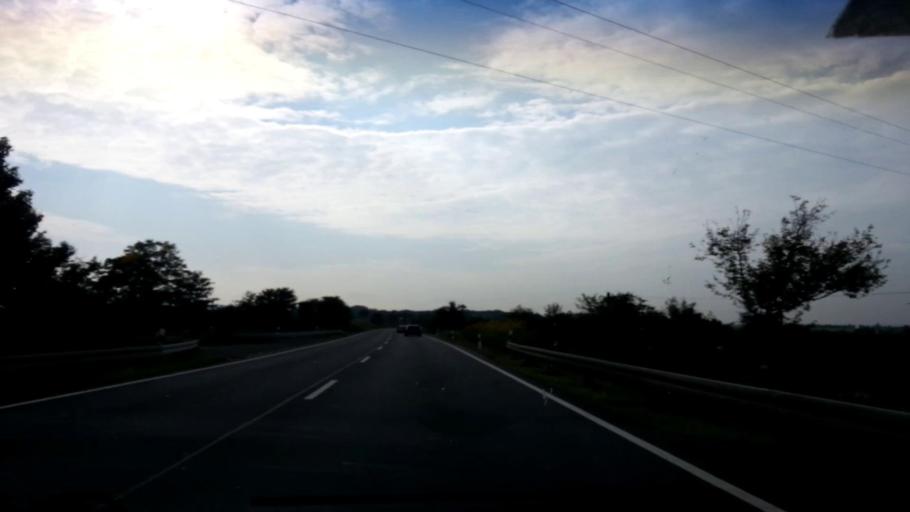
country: DE
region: Bavaria
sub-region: Regierungsbezirk Unterfranken
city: Prichsenstadt
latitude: 49.8428
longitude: 10.3512
